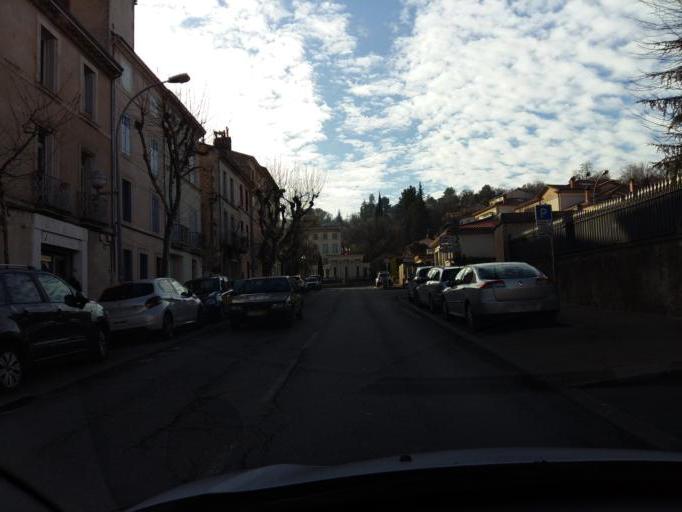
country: FR
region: Provence-Alpes-Cote d'Azur
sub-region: Departement du Vaucluse
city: Apt
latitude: 43.8754
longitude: 5.3950
